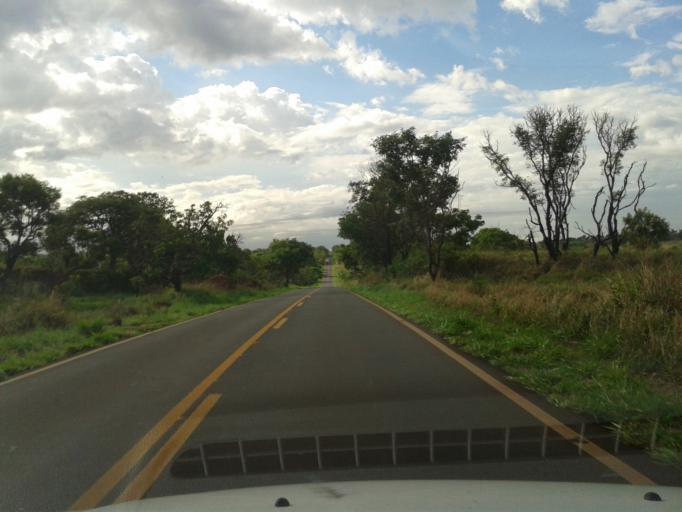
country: BR
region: Minas Gerais
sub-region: Ituiutaba
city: Ituiutaba
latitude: -19.0210
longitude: -49.7755
